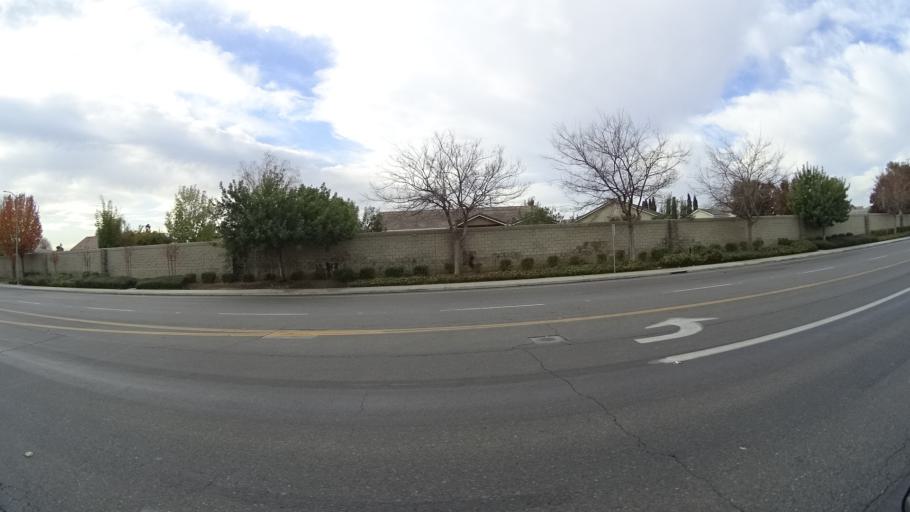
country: US
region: California
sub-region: Kern County
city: Greenacres
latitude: 35.4191
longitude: -119.1238
